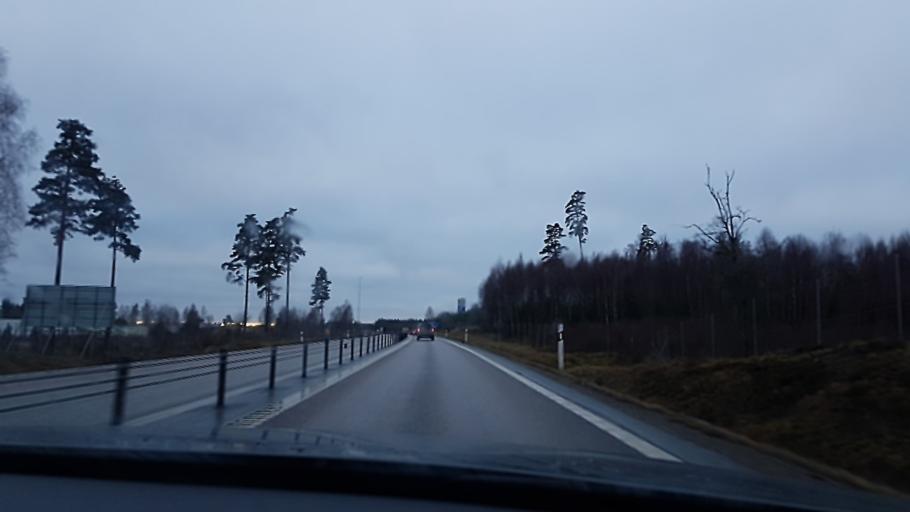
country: SE
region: Kronoberg
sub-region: Ljungby Kommun
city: Lagan
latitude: 56.9222
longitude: 13.9748
